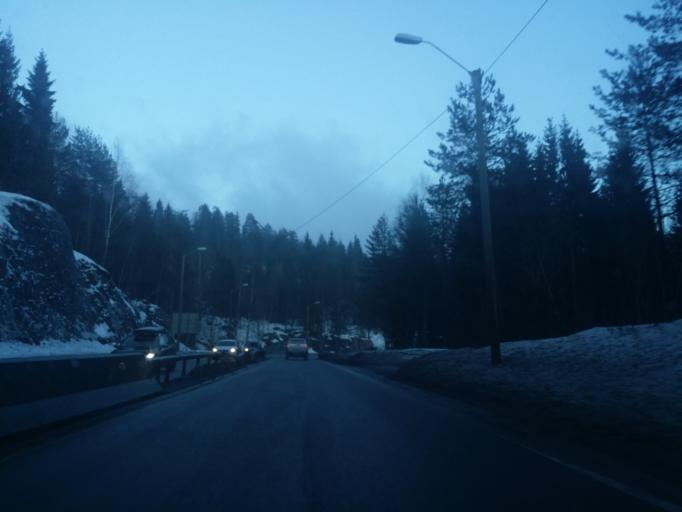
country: NO
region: Buskerud
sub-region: Hole
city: Vik
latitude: 59.9759
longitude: 10.3293
